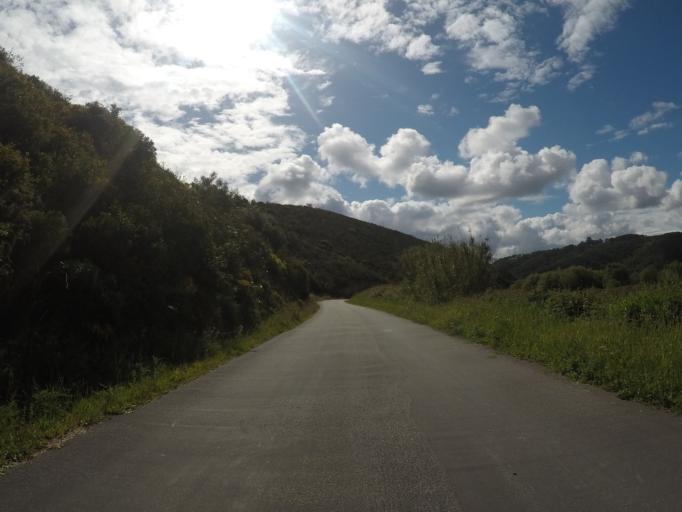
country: PT
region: Beja
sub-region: Odemira
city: Sao Teotonio
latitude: 37.4382
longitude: -8.7884
